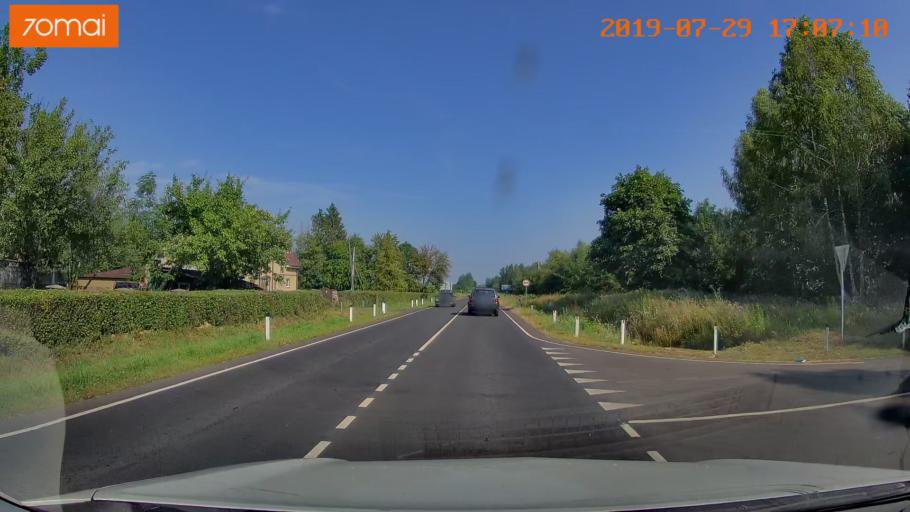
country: RU
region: Kaliningrad
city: Vzmorye
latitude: 54.8181
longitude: 20.3182
